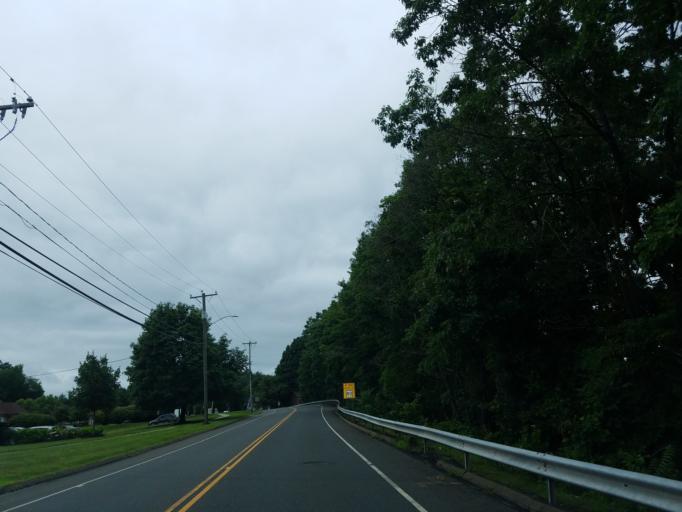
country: US
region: Connecticut
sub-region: New Haven County
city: Branford
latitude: 41.2911
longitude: -72.8192
